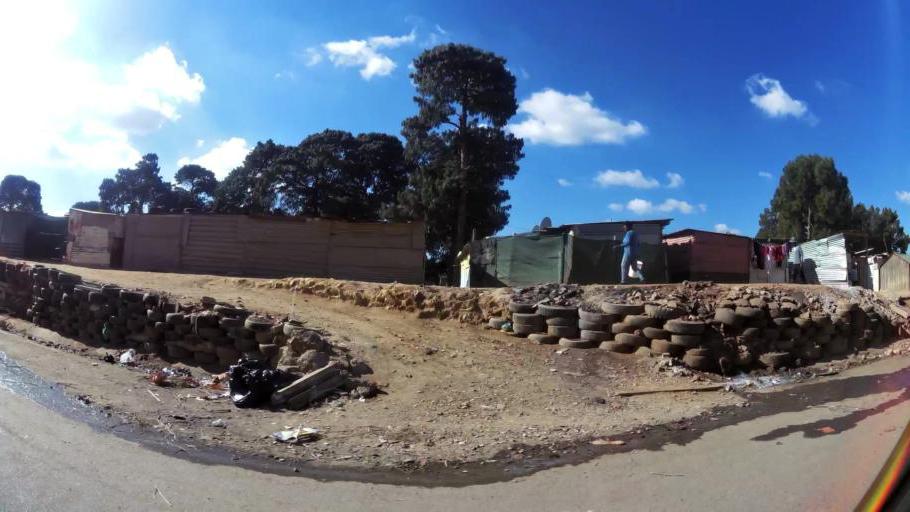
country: ZA
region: Gauteng
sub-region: West Rand District Municipality
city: Muldersdriseloop
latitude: -26.0542
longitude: 27.9046
